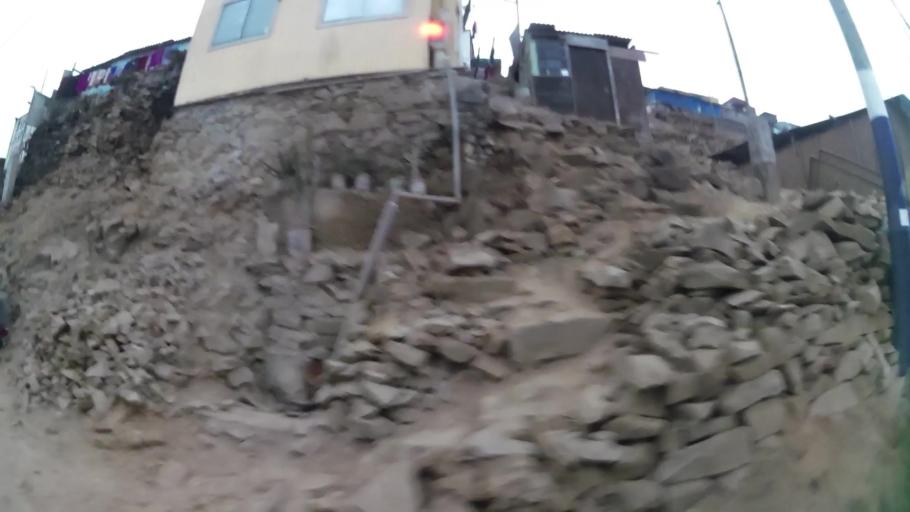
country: PE
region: Lima
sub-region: Lima
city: Surco
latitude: -12.1897
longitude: -77.0206
